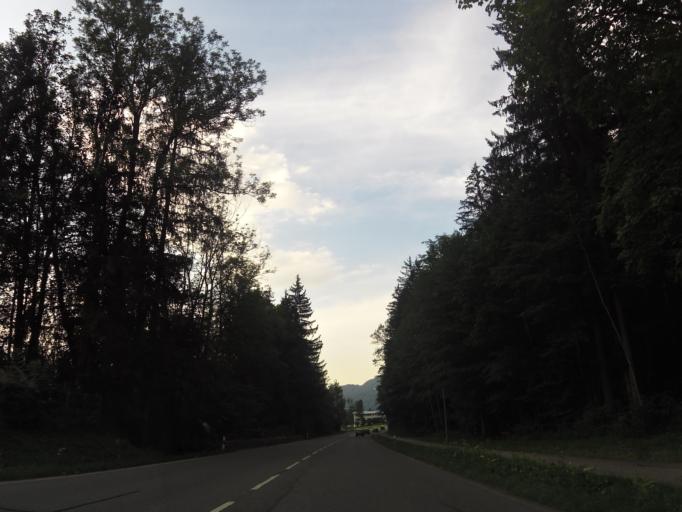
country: DE
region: Bavaria
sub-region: Upper Bavaria
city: Schoenau am Koenigssee
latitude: 47.6009
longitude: 12.9897
